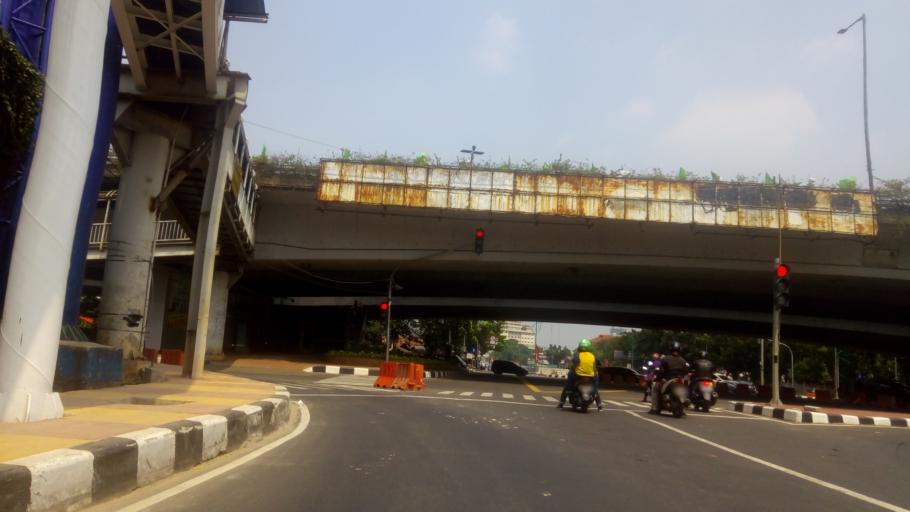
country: ID
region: Jakarta Raya
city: Jakarta
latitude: -6.2362
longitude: 106.8282
